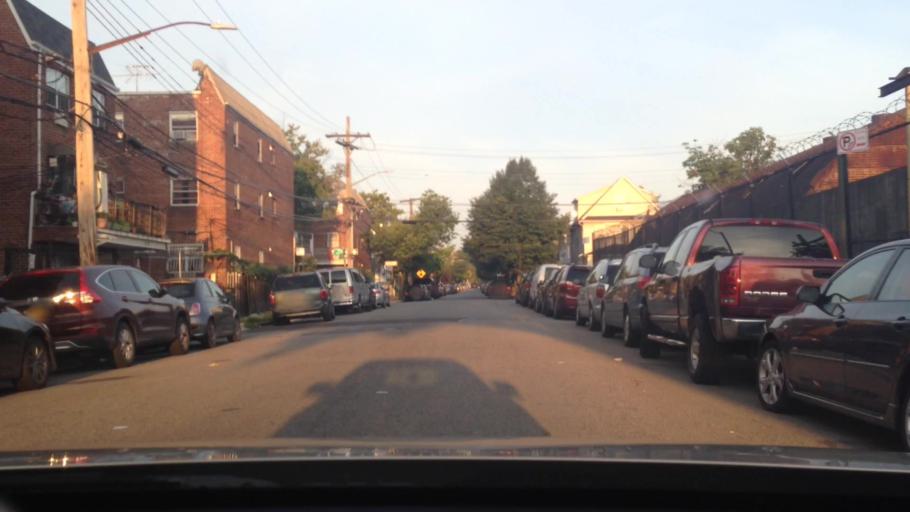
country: US
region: New York
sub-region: Queens County
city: Borough of Queens
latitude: 40.7391
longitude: -73.8630
